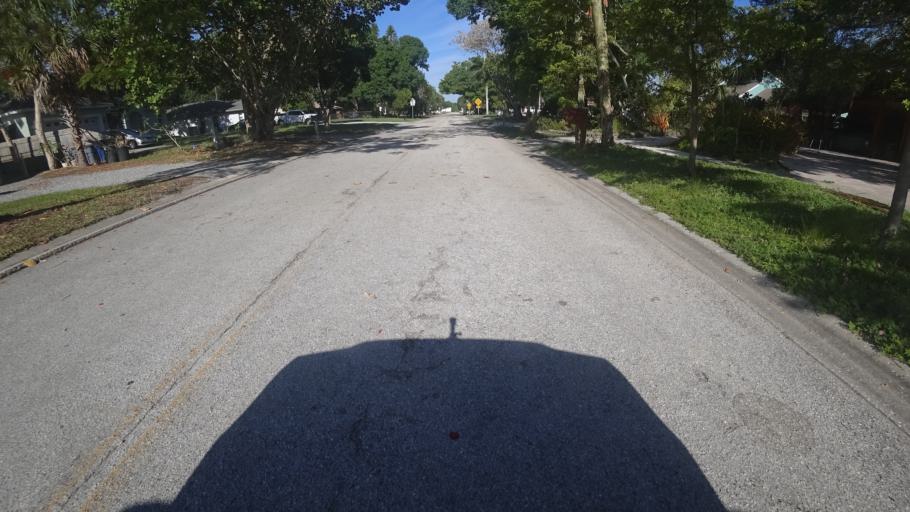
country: US
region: Florida
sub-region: Manatee County
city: West Bradenton
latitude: 27.5123
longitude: -82.6374
